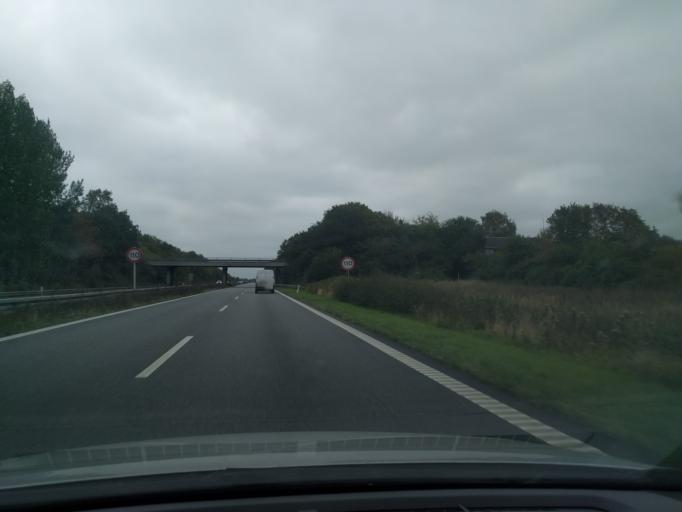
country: DK
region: Zealand
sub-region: Slagelse Kommune
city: Korsor
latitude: 55.3604
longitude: 11.1709
